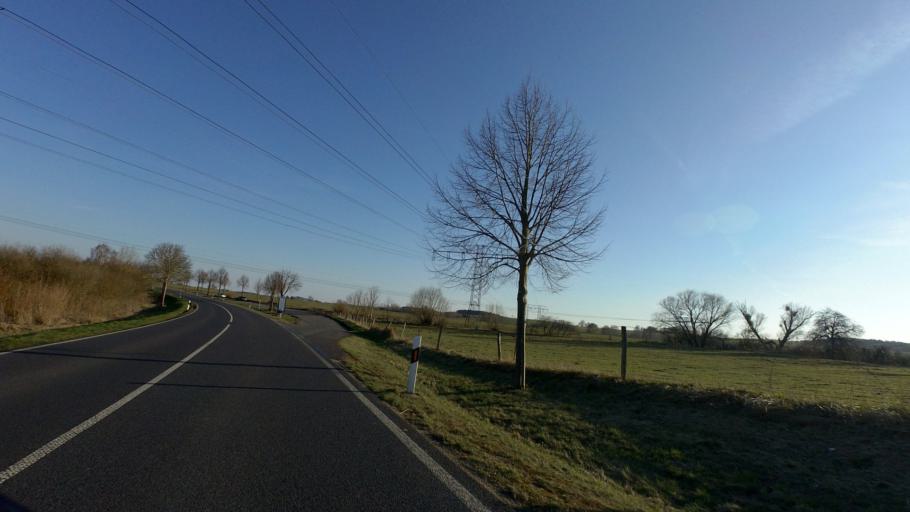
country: DE
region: Brandenburg
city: Britz
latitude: 52.9205
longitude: 13.7972
